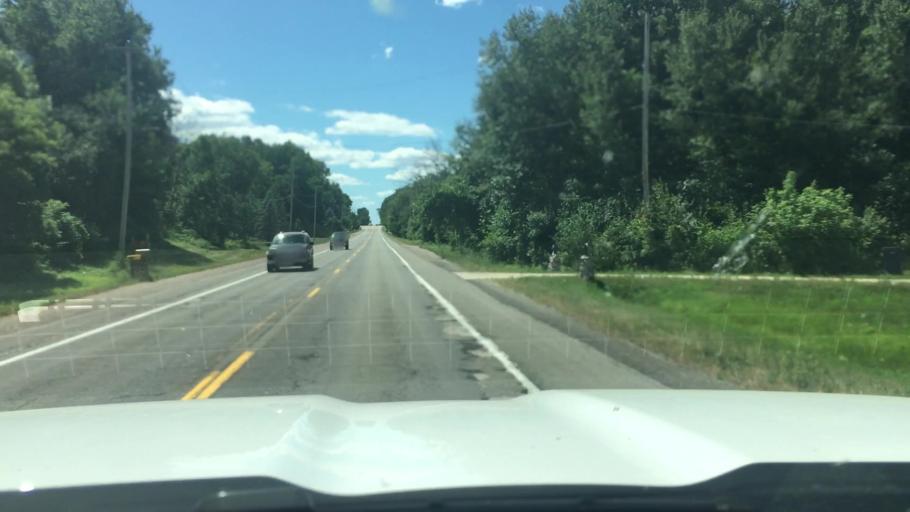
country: US
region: Michigan
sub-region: Kent County
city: Sparta
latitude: 43.1607
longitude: -85.6323
